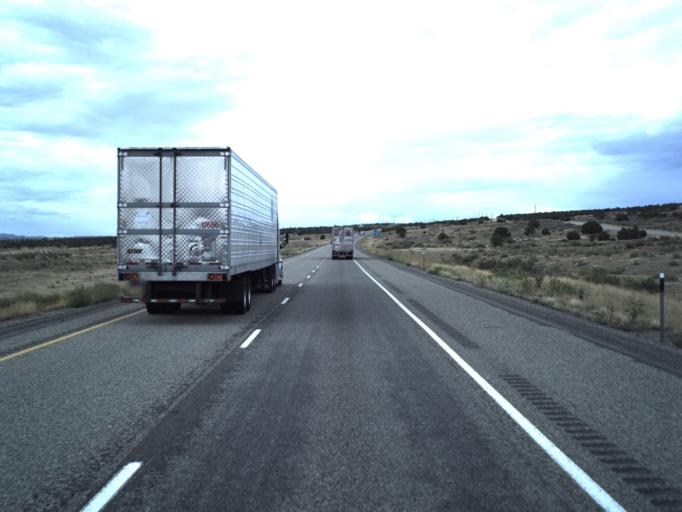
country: US
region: Colorado
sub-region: Mesa County
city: Loma
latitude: 39.1538
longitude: -109.1459
